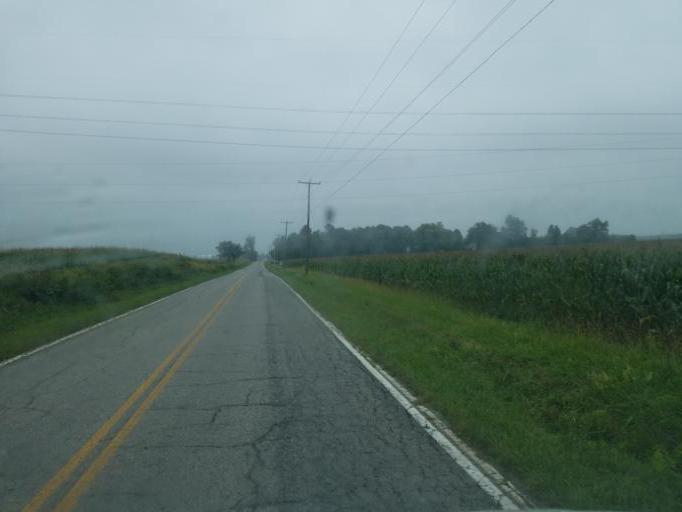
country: US
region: Ohio
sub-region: Knox County
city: Centerburg
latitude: 40.2624
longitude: -82.6916
